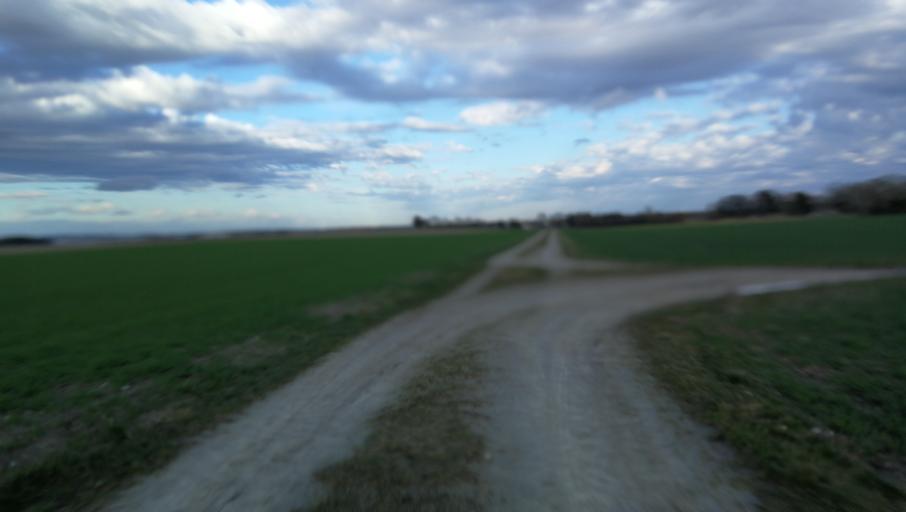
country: DE
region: Bavaria
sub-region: Upper Bavaria
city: Fuerstenfeldbruck
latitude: 48.1999
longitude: 11.2170
